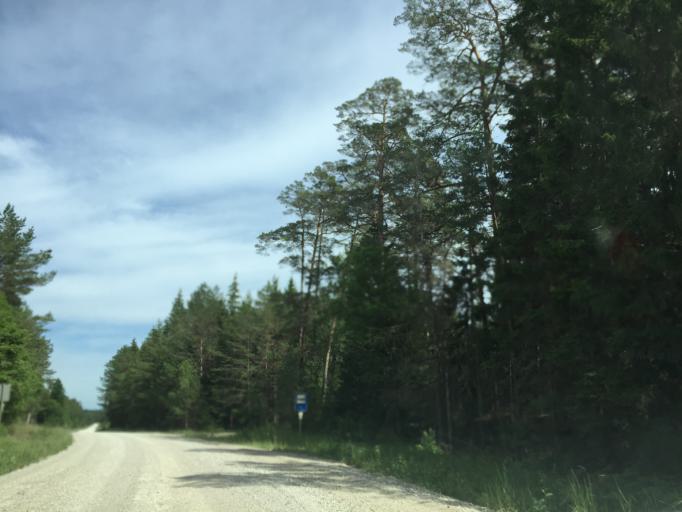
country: LV
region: Dundaga
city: Dundaga
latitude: 57.6217
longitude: 22.5576
